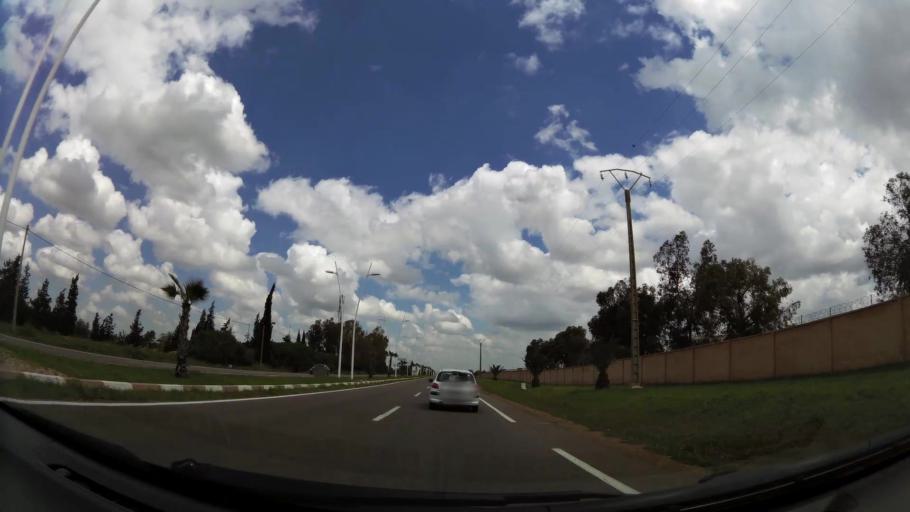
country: MA
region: Chaouia-Ouardigha
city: Nouaseur
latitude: 33.3972
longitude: -7.5848
